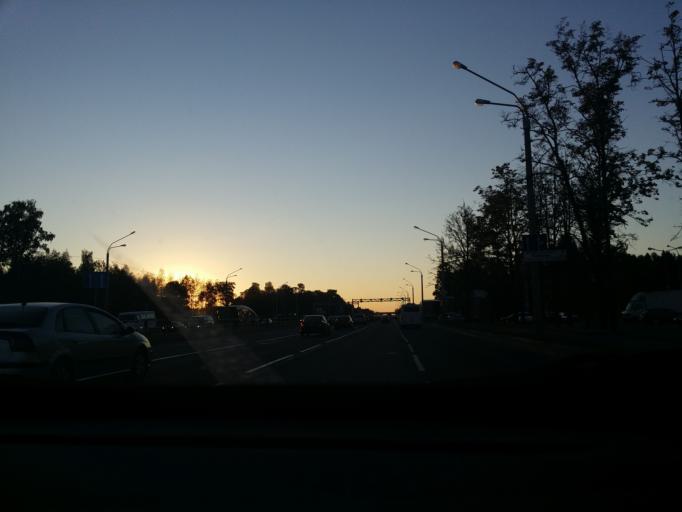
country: BY
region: Minsk
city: Vyaliki Trastsyanets
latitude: 53.8481
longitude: 27.7062
